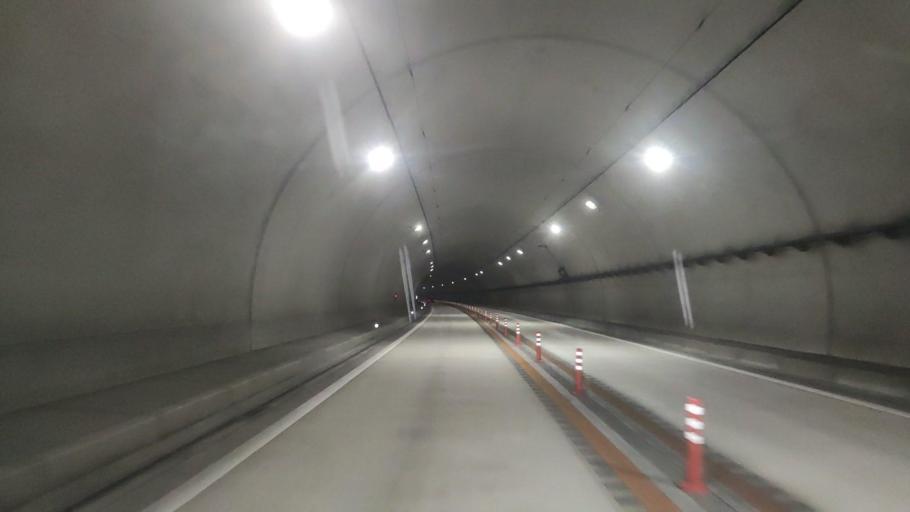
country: JP
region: Wakayama
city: Tanabe
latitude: 33.5623
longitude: 135.5027
